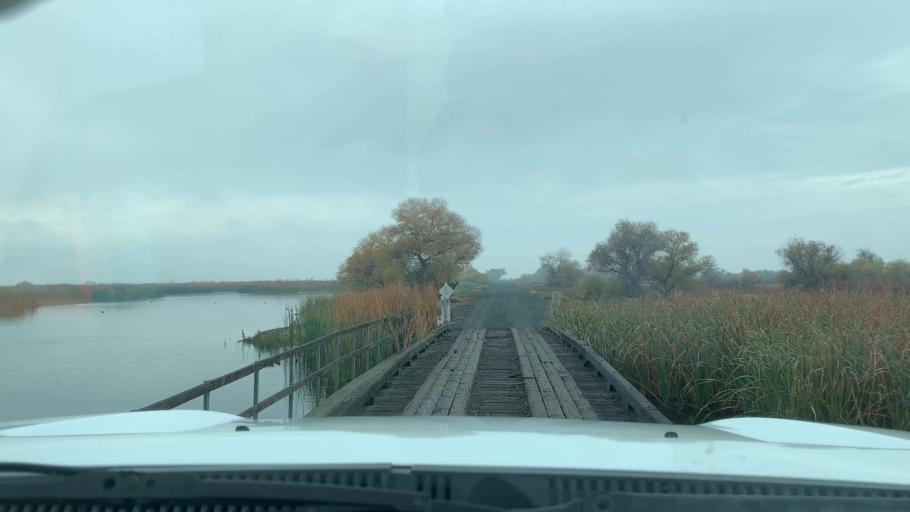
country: US
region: California
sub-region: Kern County
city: Lost Hills
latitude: 35.7336
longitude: -119.5960
